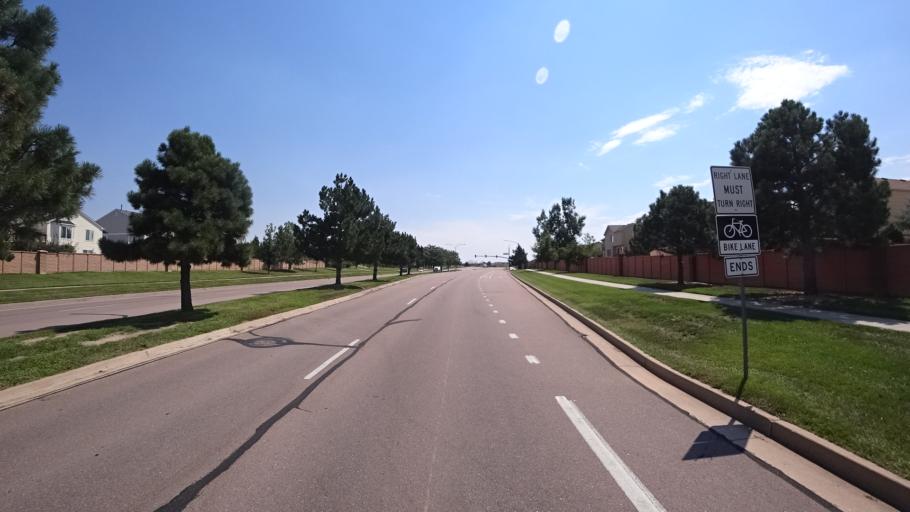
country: US
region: Colorado
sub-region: El Paso County
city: Cimarron Hills
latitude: 38.9293
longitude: -104.7300
